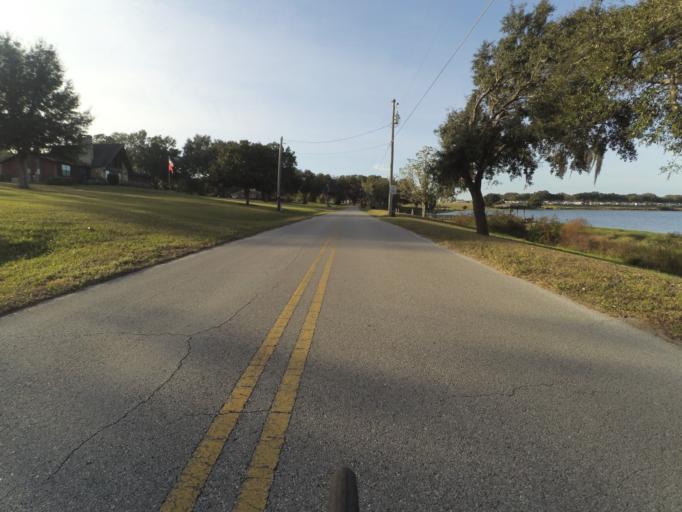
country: US
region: Florida
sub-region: Lake County
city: Umatilla
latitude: 28.9415
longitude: -81.6561
